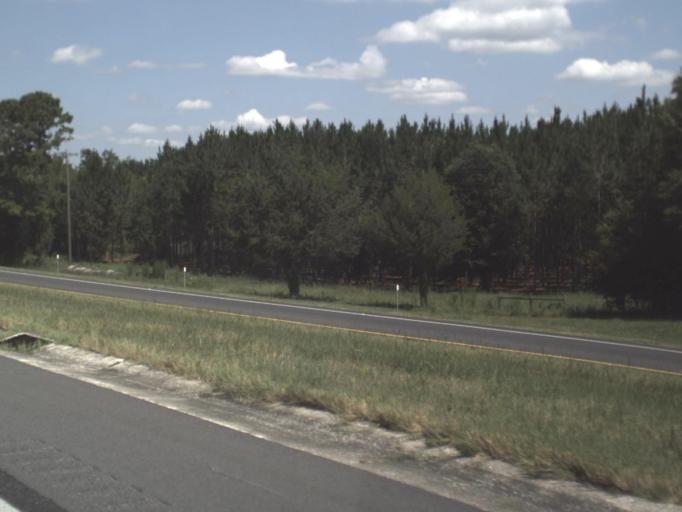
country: US
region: Florida
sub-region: Madison County
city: Madison
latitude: 30.3805
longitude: -83.3001
